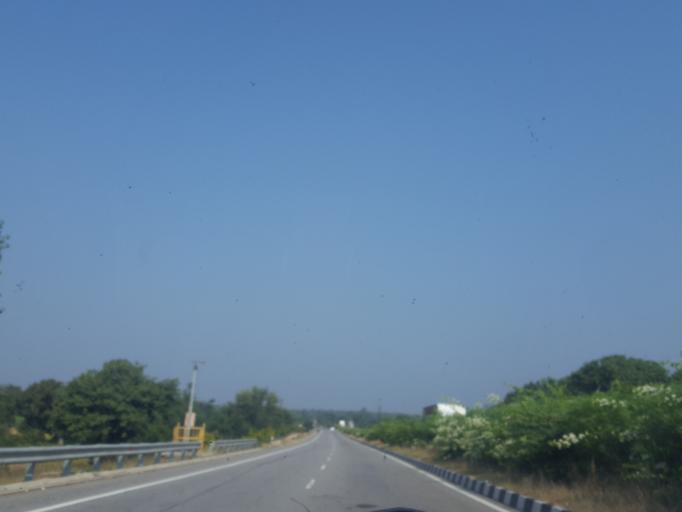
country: IN
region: Telangana
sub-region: Nizamabad District
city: Kamareddi
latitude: 18.4182
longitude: 78.2591
